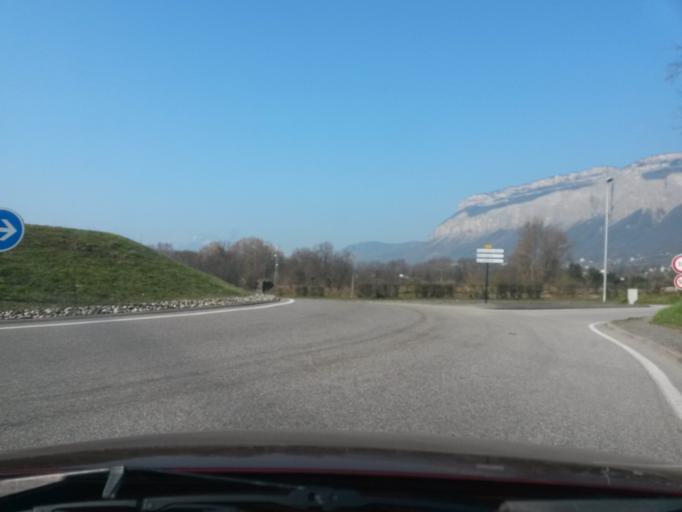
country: FR
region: Rhone-Alpes
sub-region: Departement de l'Isere
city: Saint-Nazaire-les-Eymes
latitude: 45.2410
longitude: 5.8469
